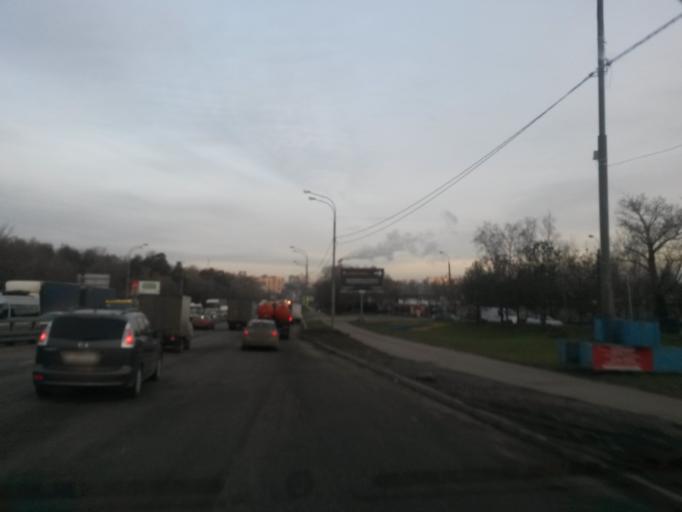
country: RU
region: Moskovskaya
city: Bol'shaya Setun'
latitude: 55.7053
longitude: 37.4210
